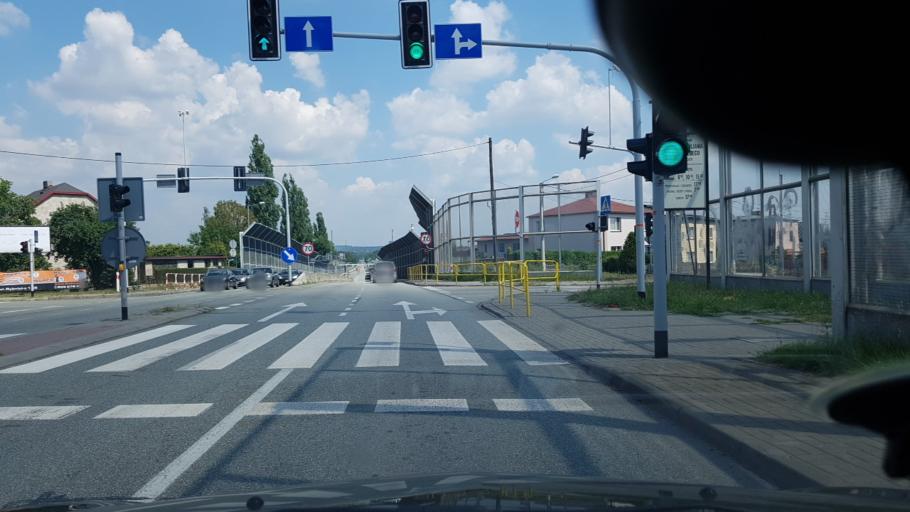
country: PL
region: Silesian Voivodeship
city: Gardawice
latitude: 50.1084
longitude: 18.7923
